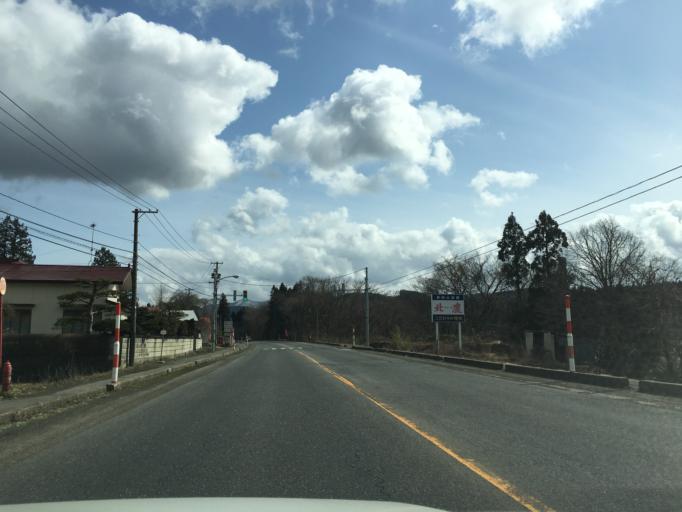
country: JP
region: Akita
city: Odate
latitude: 40.2260
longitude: 140.6008
